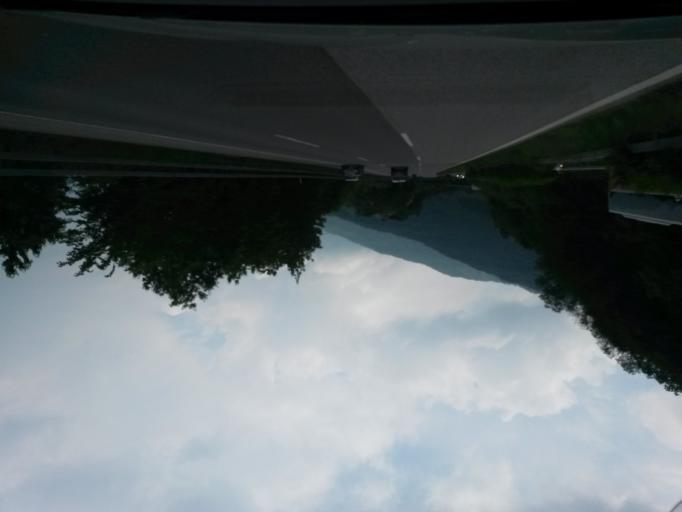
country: CH
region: Ticino
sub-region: Bellinzona District
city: Camorino
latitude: 46.1569
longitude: 8.9885
